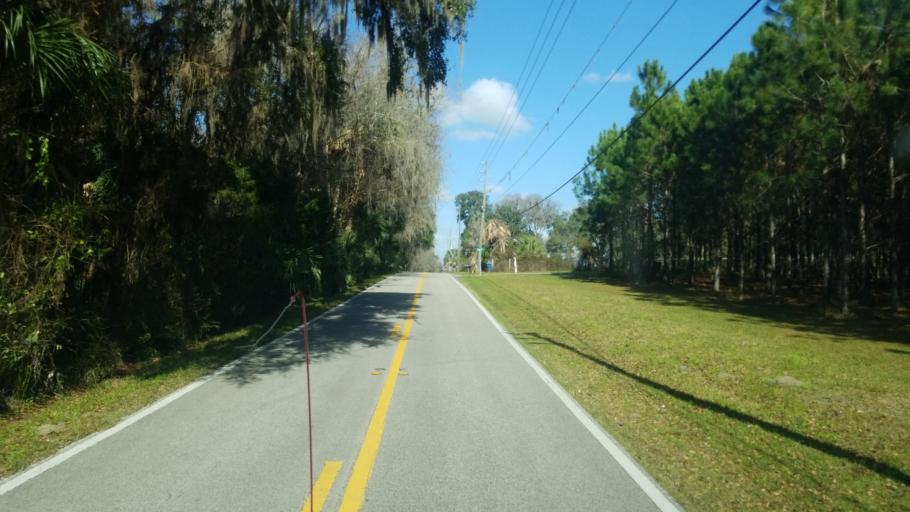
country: US
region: Florida
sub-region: Hernando County
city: North Brooksville
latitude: 28.6166
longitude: -82.3801
